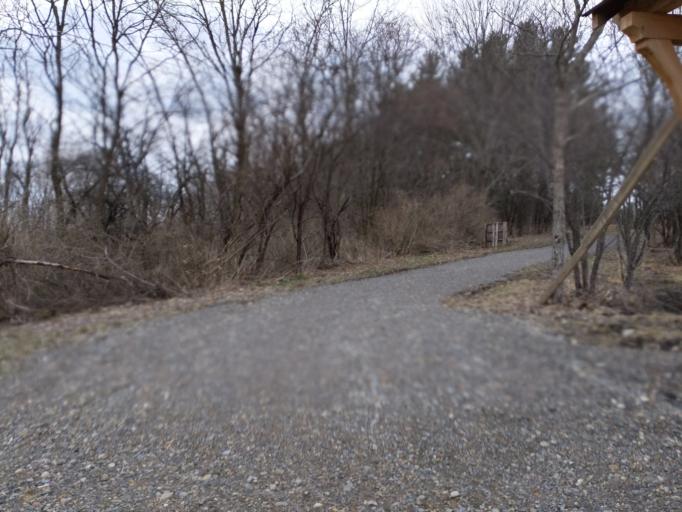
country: US
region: New York
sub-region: Tompkins County
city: Dryden
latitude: 42.4985
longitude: -76.3288
